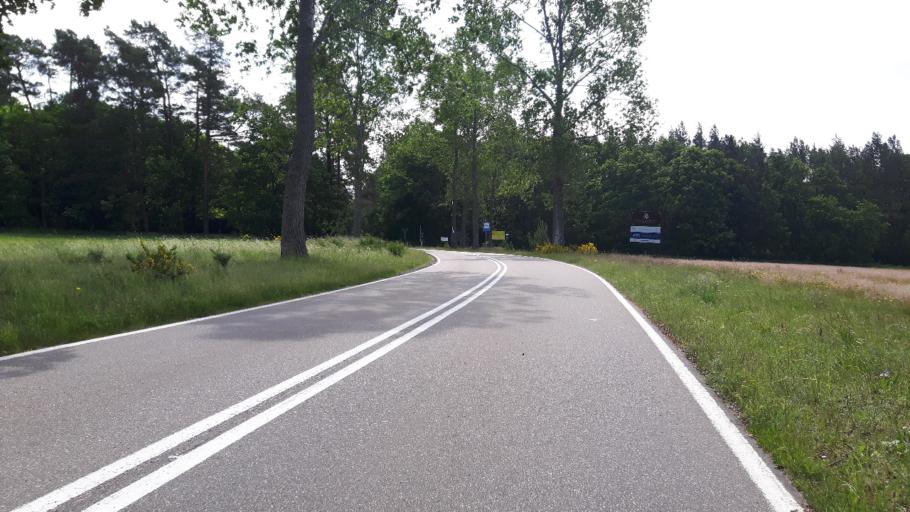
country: PL
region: Pomeranian Voivodeship
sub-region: Powiat leborski
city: Leba
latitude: 54.7447
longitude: 17.7127
